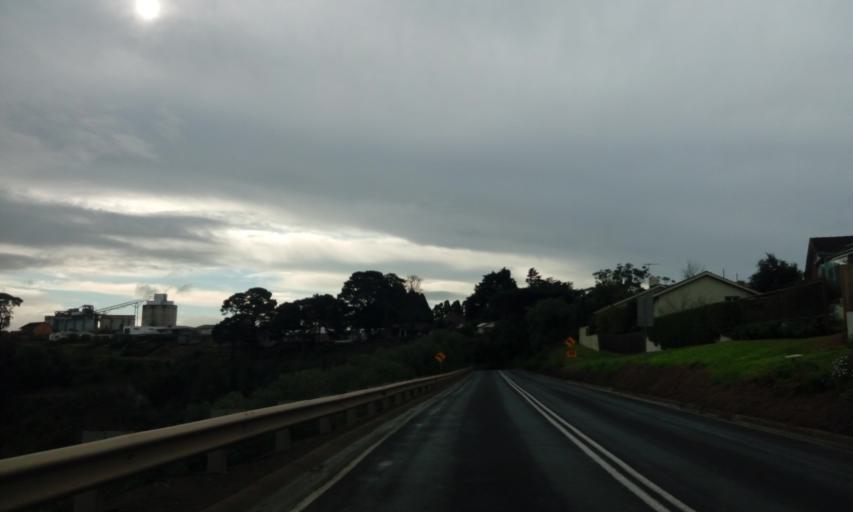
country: AU
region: Victoria
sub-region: Greater Geelong
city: Hamlyn Heights
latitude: -38.1433
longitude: 144.3233
